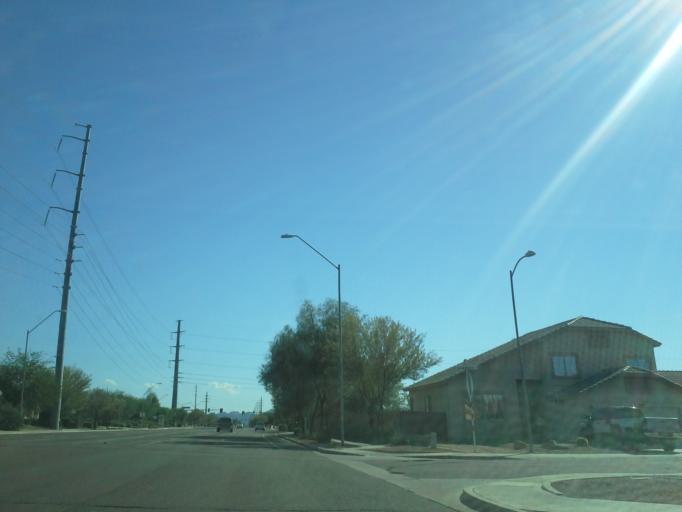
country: US
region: Arizona
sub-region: Maricopa County
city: Paradise Valley
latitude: 33.6576
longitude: -112.0137
